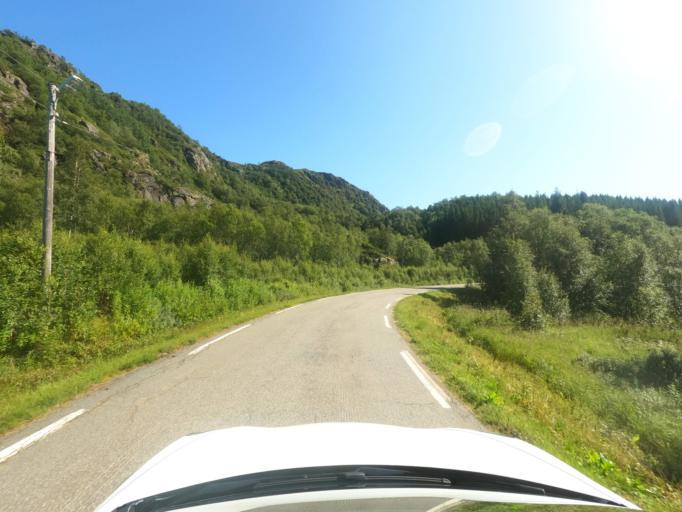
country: NO
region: Nordland
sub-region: Hadsel
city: Stokmarknes
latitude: 68.3064
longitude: 15.0910
